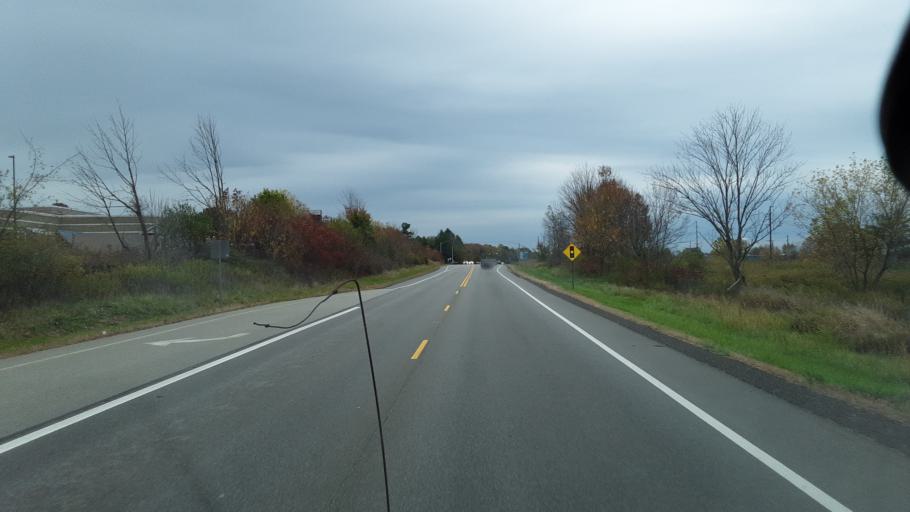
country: US
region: Ohio
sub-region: Portage County
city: Ravenna
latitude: 41.1794
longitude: -81.2510
